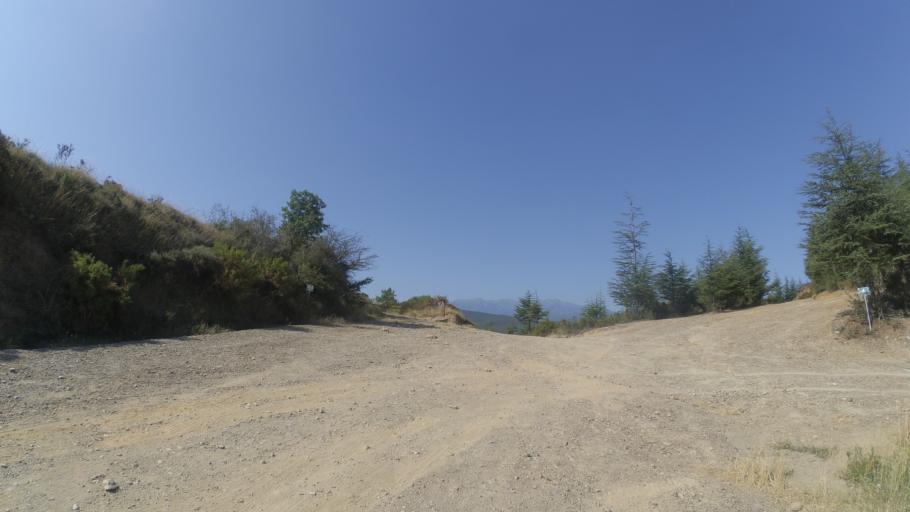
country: FR
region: Languedoc-Roussillon
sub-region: Departement des Pyrenees-Orientales
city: Millas
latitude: 42.6266
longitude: 2.6756
